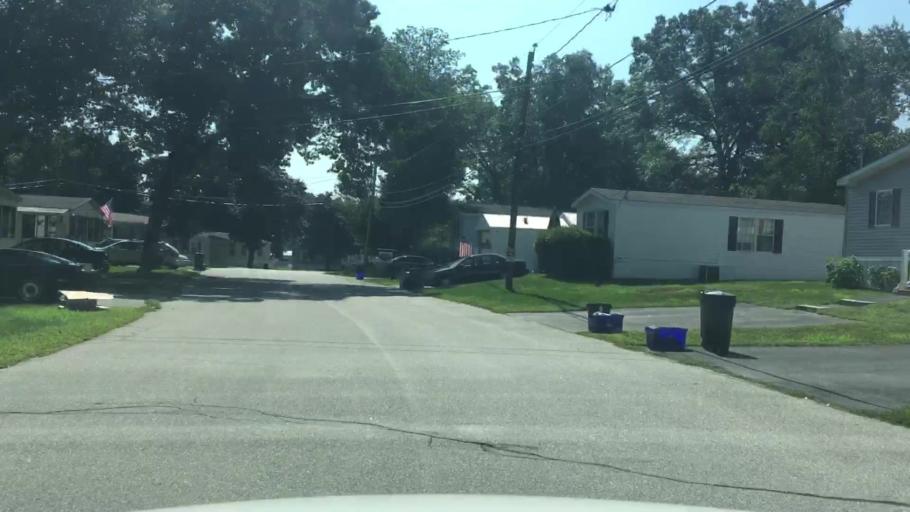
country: US
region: New Hampshire
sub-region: Rockingham County
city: Hampstead
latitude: 42.8829
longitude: -71.1620
